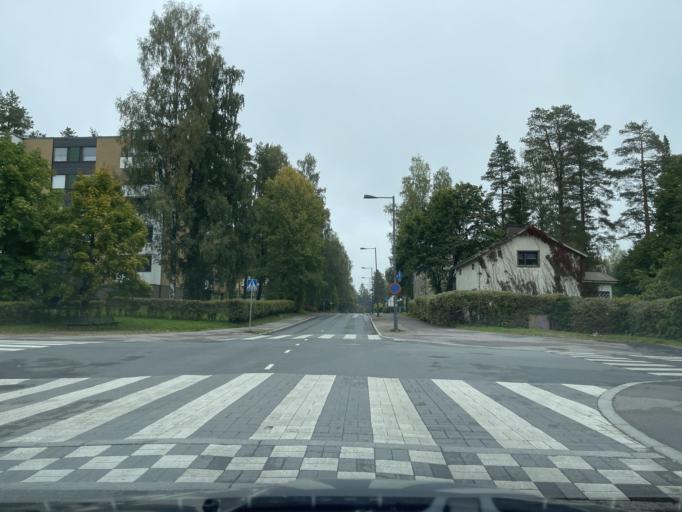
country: FI
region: Uusimaa
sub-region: Helsinki
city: Hyvinge
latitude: 60.6228
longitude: 24.8547
